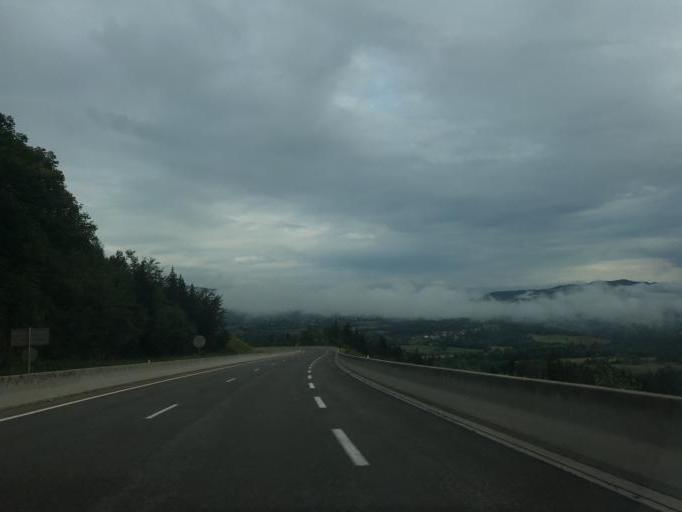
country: FR
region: Rhone-Alpes
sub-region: Departement de l'Ain
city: Arbent
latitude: 46.2879
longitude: 5.6598
